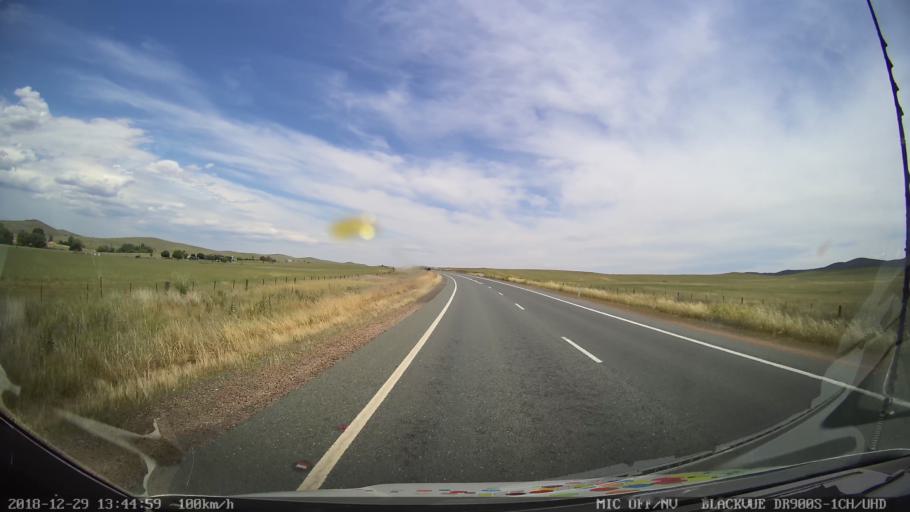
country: AU
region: New South Wales
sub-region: Cooma-Monaro
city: Cooma
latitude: -36.0895
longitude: 149.1457
